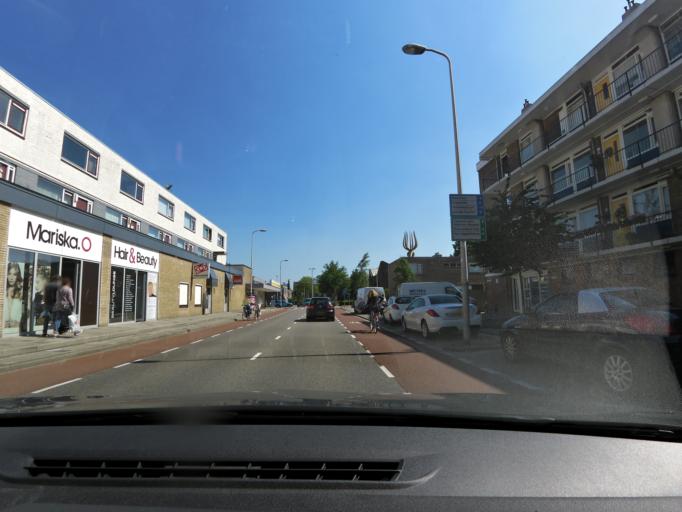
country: NL
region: South Holland
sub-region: Gemeente Capelle aan den IJssel
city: Capelle aan den IJssel
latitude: 51.9292
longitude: 4.5892
